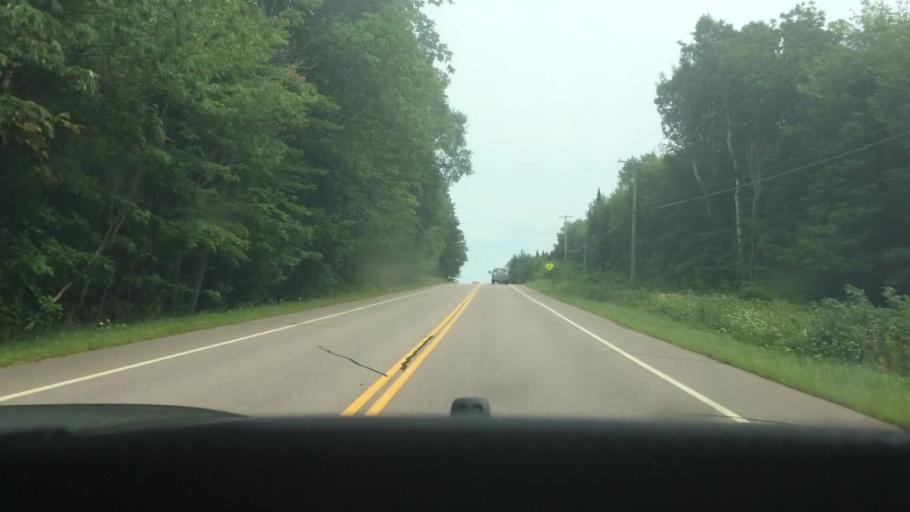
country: US
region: New York
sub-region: Franklin County
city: Malone
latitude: 44.8533
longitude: -74.0741
